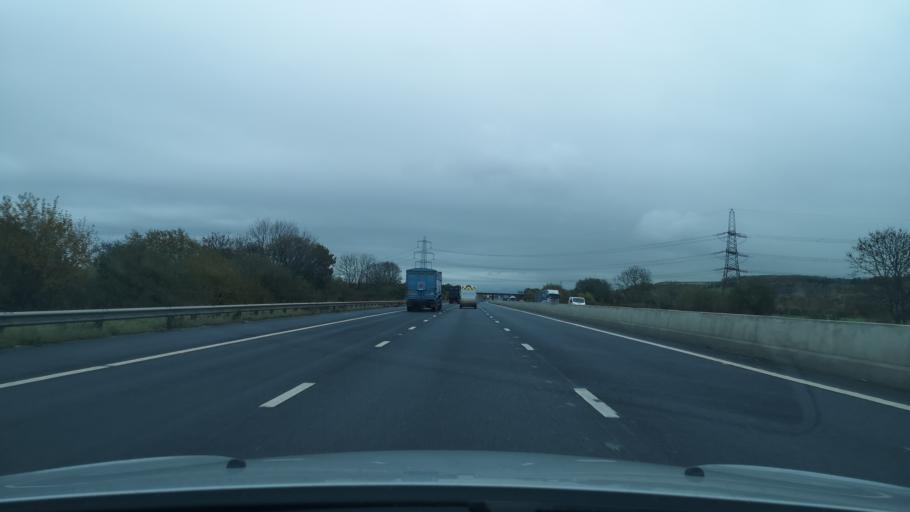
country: GB
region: England
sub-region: City and Borough of Wakefield
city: Knottingley
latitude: 53.6951
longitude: -1.2069
